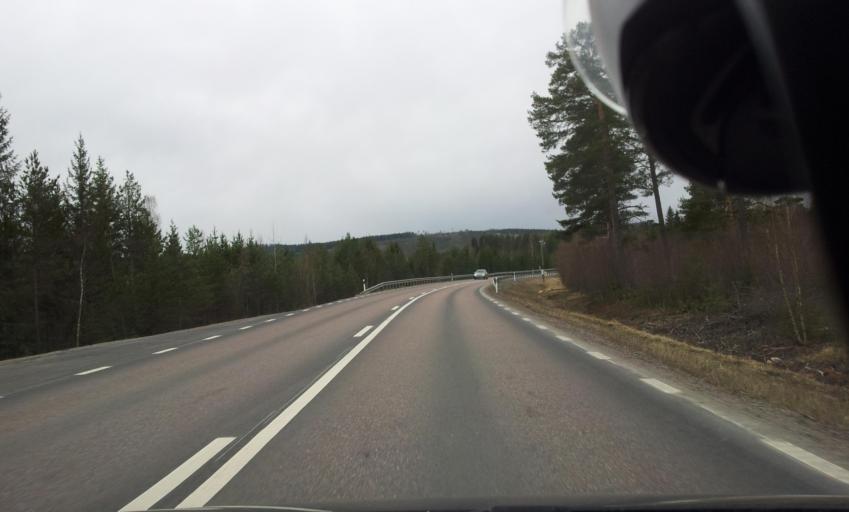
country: SE
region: Gaevleborg
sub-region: Ljusdals Kommun
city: Ljusdal
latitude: 61.8202
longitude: 16.0259
